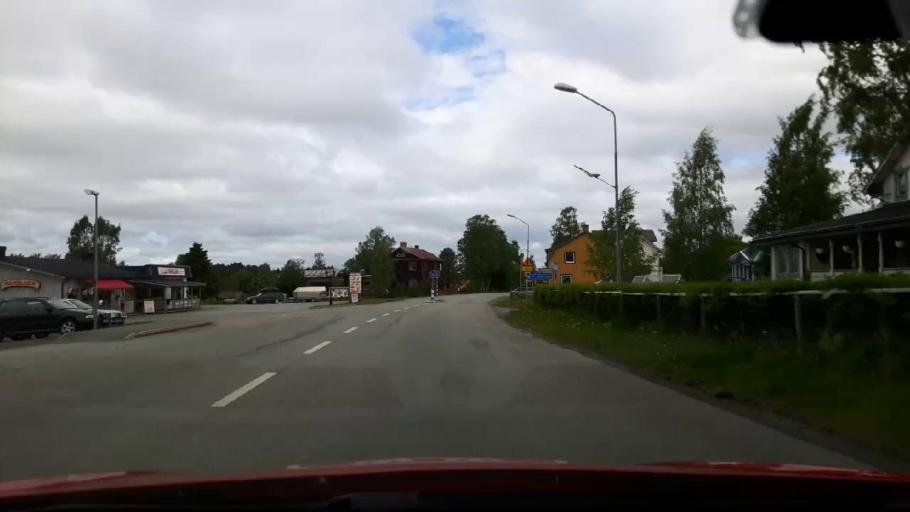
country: SE
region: Jaemtland
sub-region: Krokoms Kommun
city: Krokom
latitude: 63.3024
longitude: 14.4725
